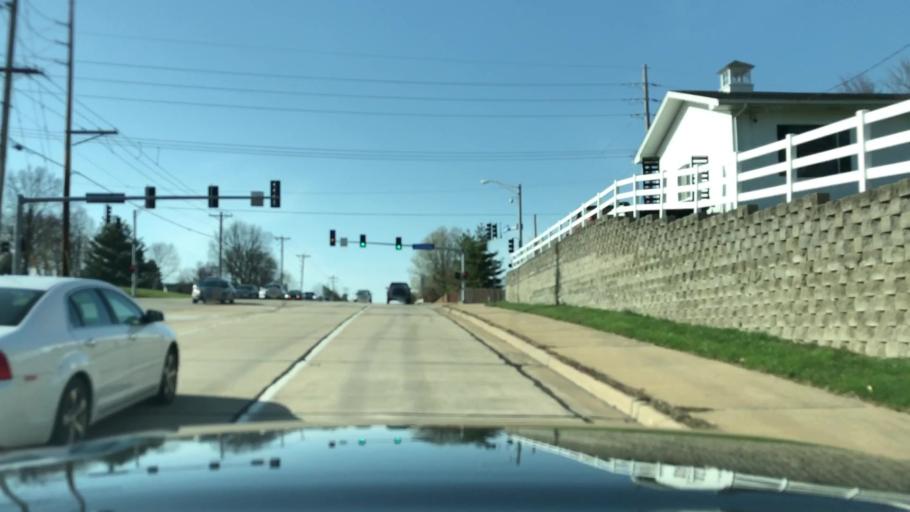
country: US
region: Missouri
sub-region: Saint Charles County
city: Saint Charles
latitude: 38.7721
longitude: -90.5495
